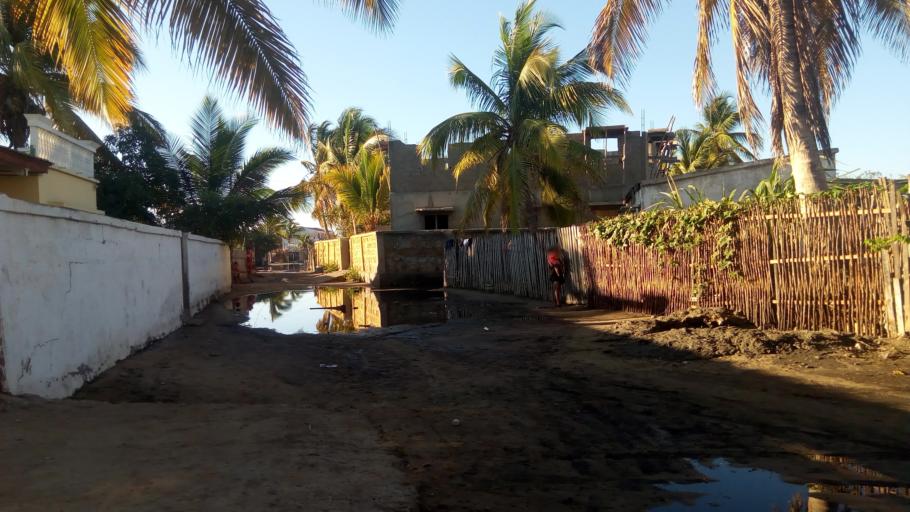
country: MG
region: Menabe
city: Morondava
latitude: -20.2980
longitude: 44.2781
